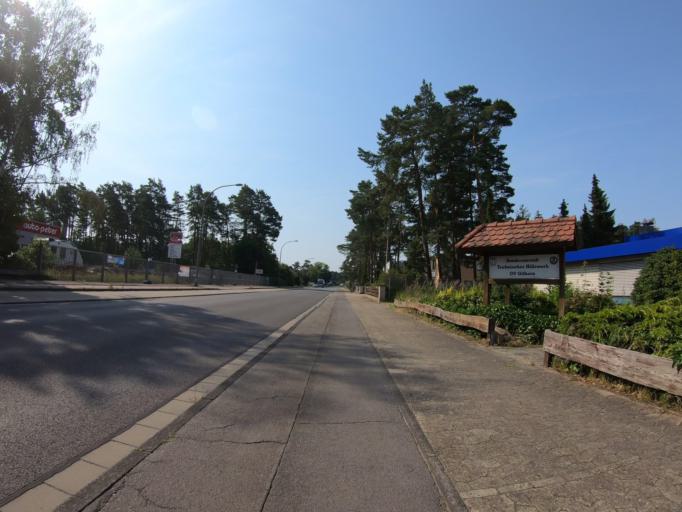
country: DE
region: Lower Saxony
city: Gifhorn
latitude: 52.4673
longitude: 10.5300
